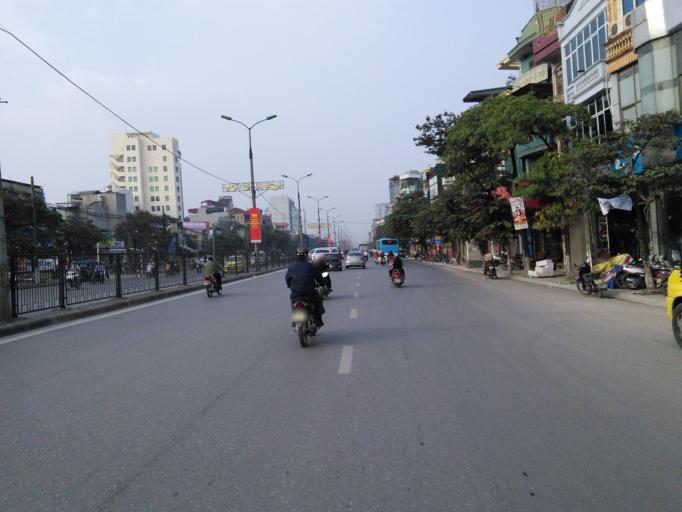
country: VN
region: Ha Noi
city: Hai BaTrung
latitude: 20.9889
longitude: 105.8412
